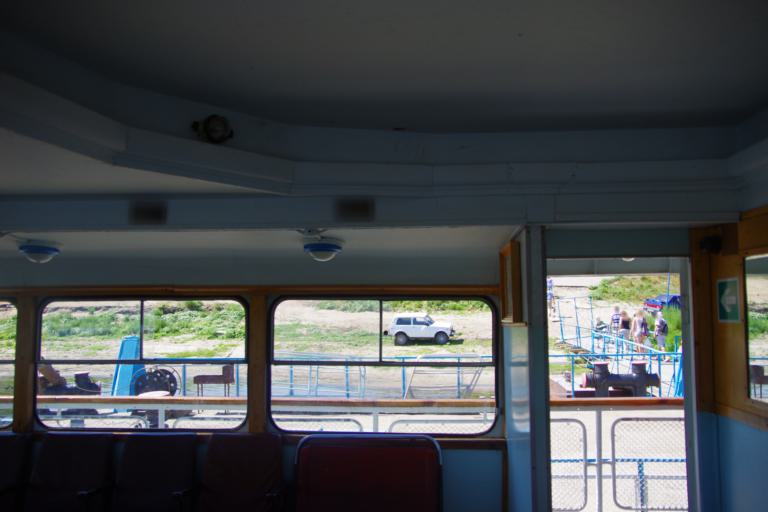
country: RU
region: Samara
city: Rozhdestveno
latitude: 53.2252
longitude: 50.0644
